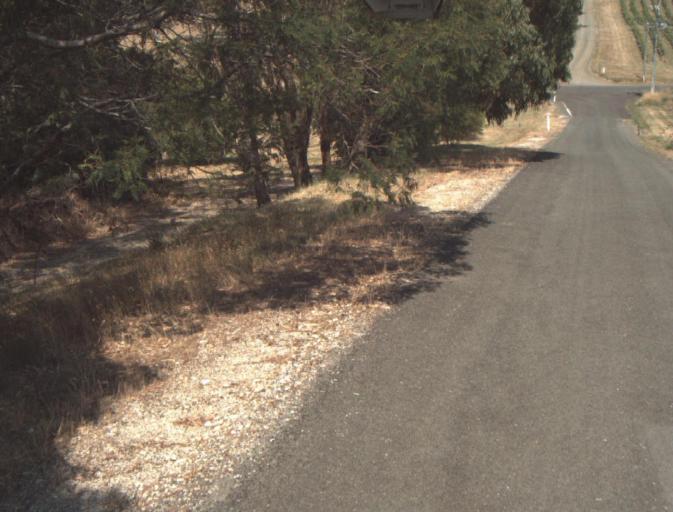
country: AU
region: Tasmania
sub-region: Launceston
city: Summerhill
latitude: -41.4981
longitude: 147.1882
